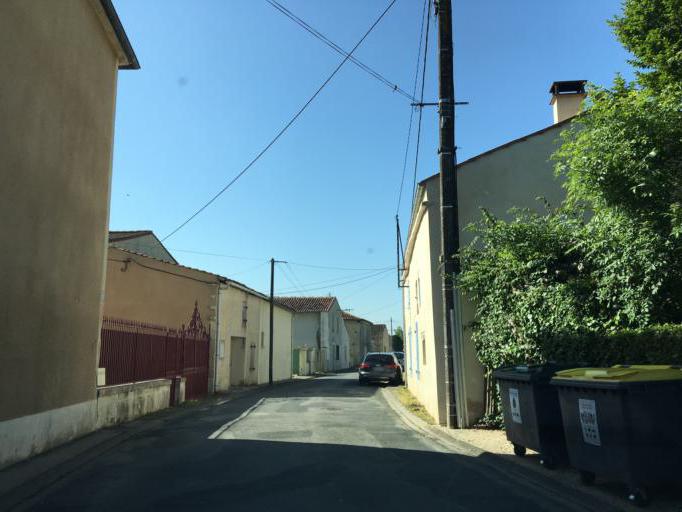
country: FR
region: Poitou-Charentes
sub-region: Departement des Deux-Sevres
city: Beauvoir-sur-Niort
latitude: 46.0964
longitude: -0.5068
